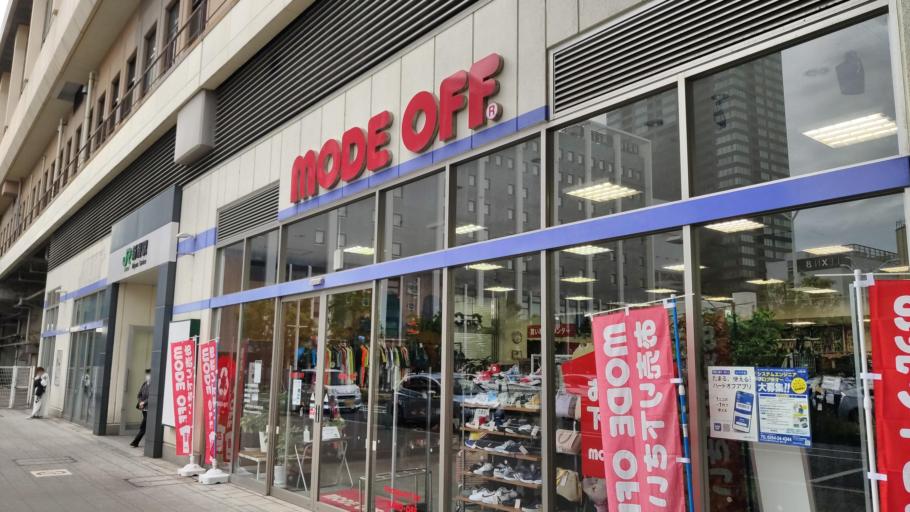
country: JP
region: Niigata
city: Niigata-shi
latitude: 37.9117
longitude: 139.0616
